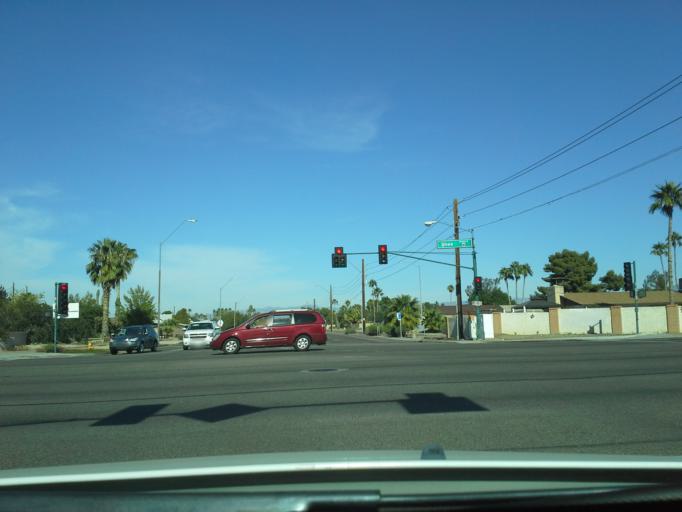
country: US
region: Arizona
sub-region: Maricopa County
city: Paradise Valley
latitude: 33.5826
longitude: -111.9957
